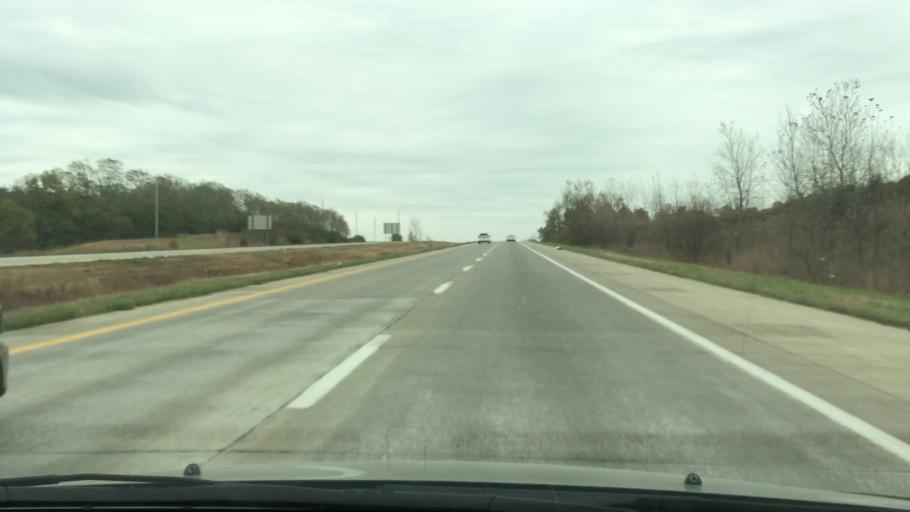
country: US
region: Missouri
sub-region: Jackson County
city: Grandview
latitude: 38.8603
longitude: -94.5728
